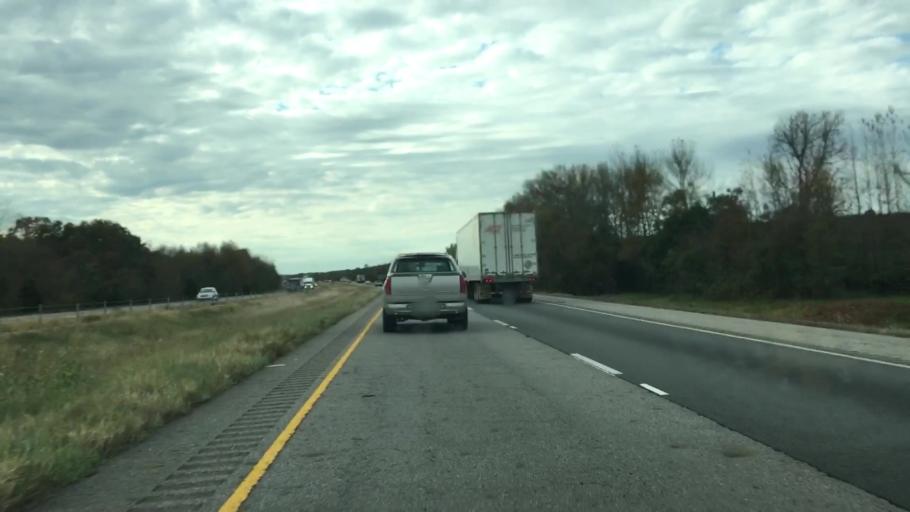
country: US
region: Arkansas
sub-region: Conway County
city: Morrilton
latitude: 35.1632
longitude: -92.6198
